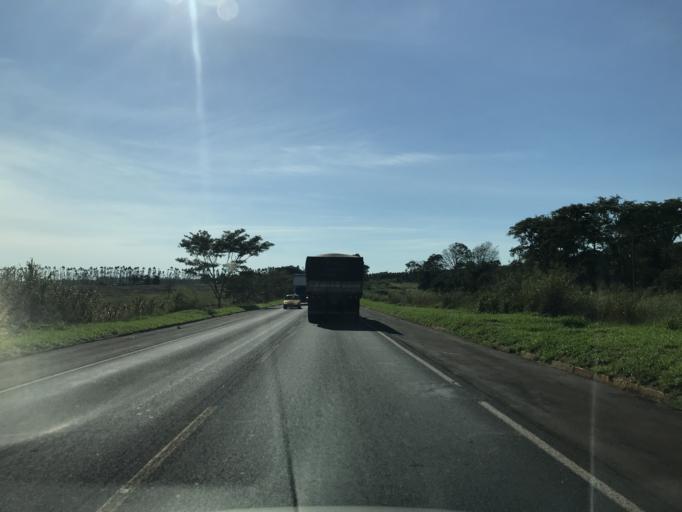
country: BR
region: Parana
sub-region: Umuarama
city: Umuarama
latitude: -23.8572
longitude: -53.3783
